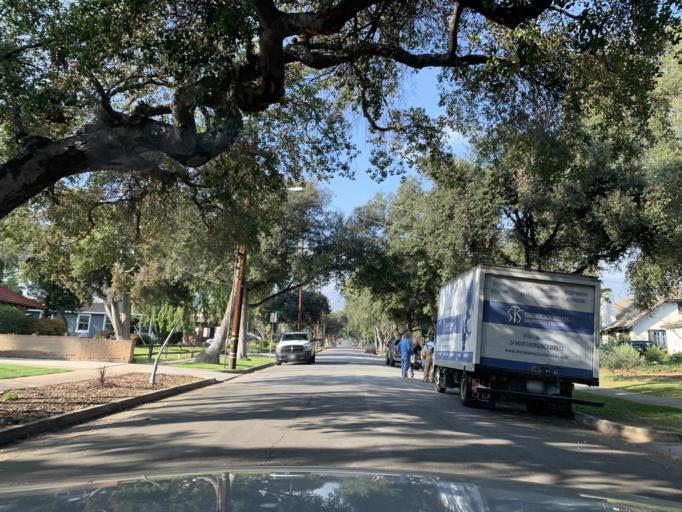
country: US
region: California
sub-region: Los Angeles County
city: Pasadena
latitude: 34.1629
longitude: -118.1244
